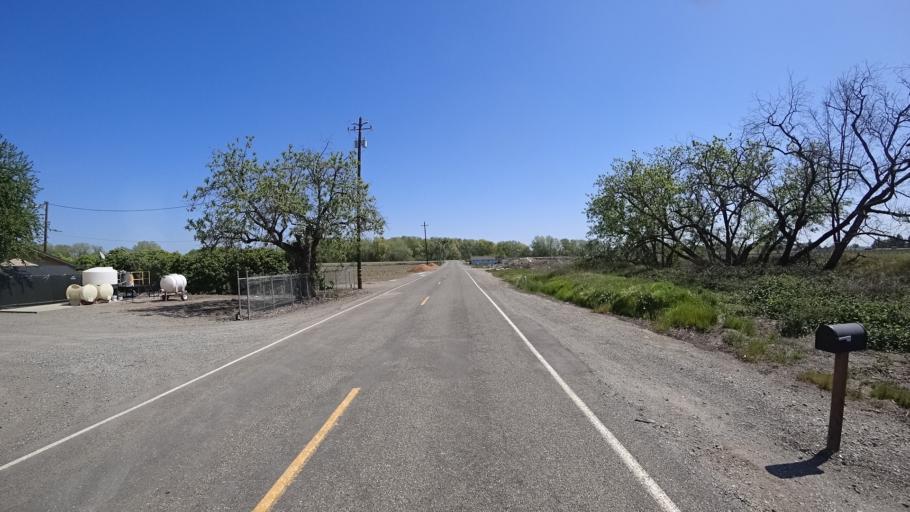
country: US
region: California
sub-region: Glenn County
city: Hamilton City
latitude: 39.5581
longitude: -122.0075
